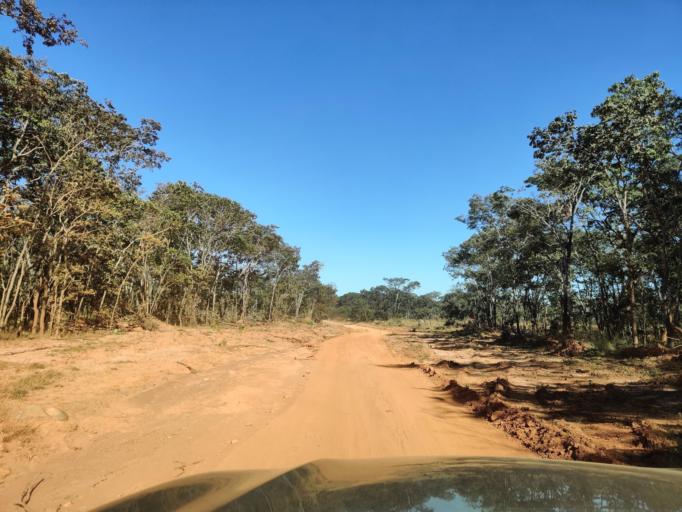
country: ZM
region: Central
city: Mkushi
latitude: -13.5111
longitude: 29.0020
